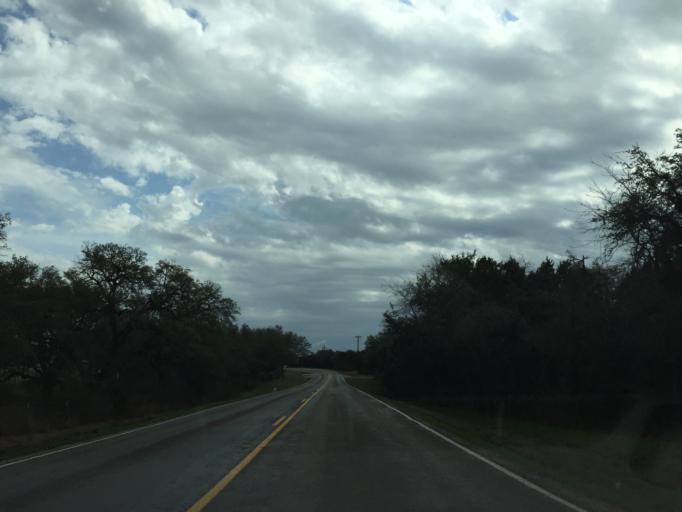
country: US
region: Texas
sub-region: Burnet County
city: Bertram
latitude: 30.6515
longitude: -97.9854
